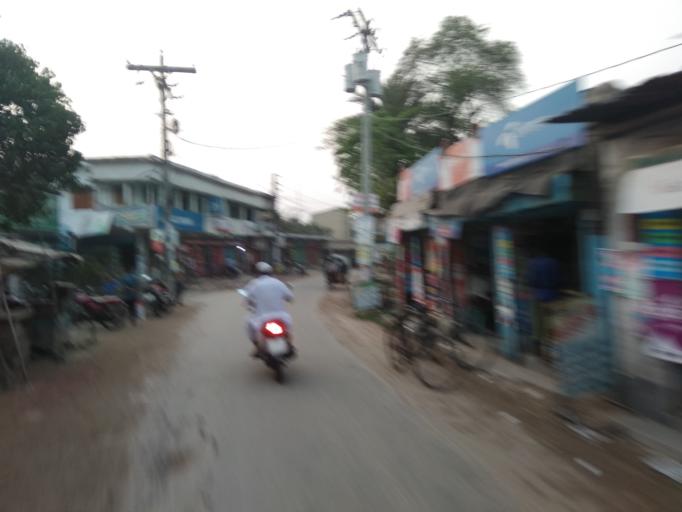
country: IN
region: West Bengal
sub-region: North 24 Parganas
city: Taki
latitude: 22.4552
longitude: 89.0317
